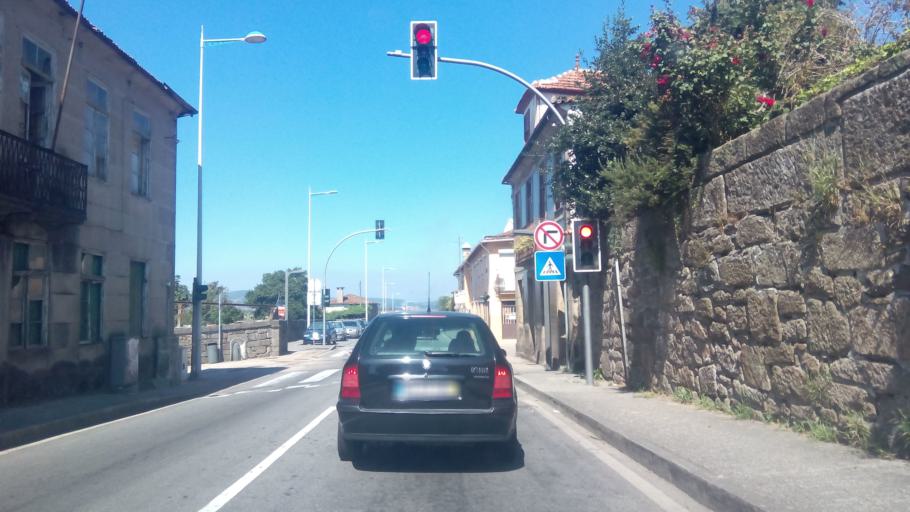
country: PT
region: Porto
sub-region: Penafiel
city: Penafiel
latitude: 41.2068
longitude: -8.2878
